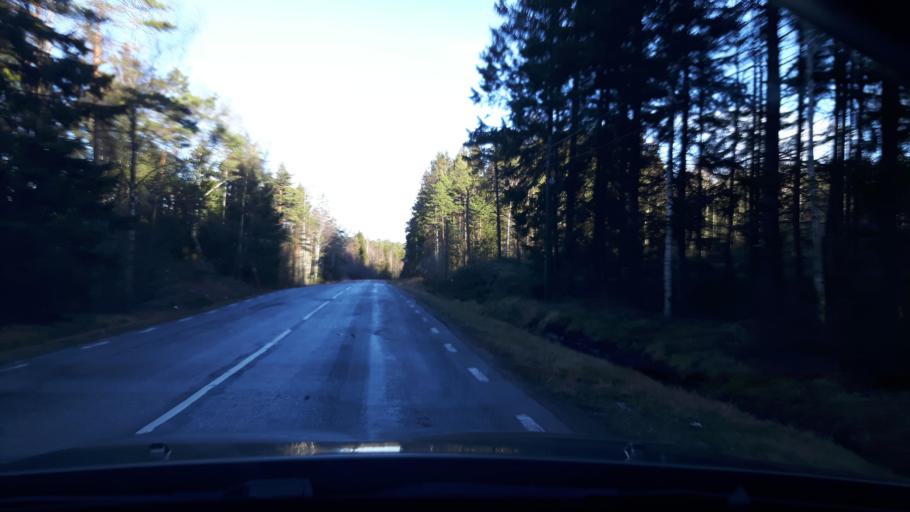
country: SE
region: Vaestra Goetaland
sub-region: Munkedals Kommun
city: Munkedal
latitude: 58.5219
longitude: 11.6857
